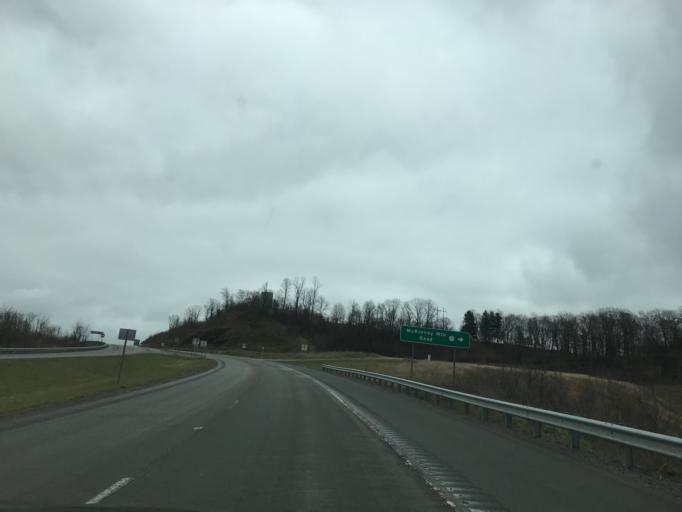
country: US
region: West Virginia
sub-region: Raleigh County
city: Sophia
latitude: 37.7102
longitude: -81.2919
